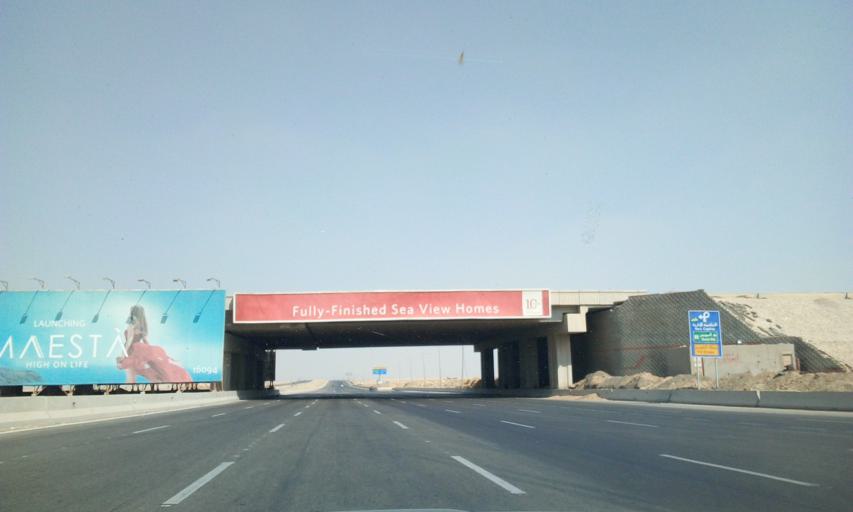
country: EG
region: Muhafazat al Qahirah
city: Halwan
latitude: 29.9059
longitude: 31.6933
